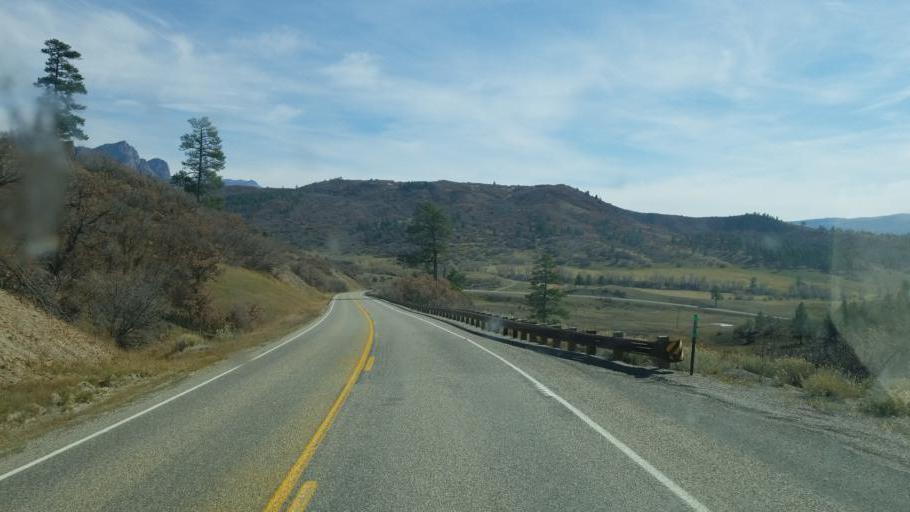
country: US
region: New Mexico
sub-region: Rio Arriba County
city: Dulce
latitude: 37.0739
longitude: -106.8335
